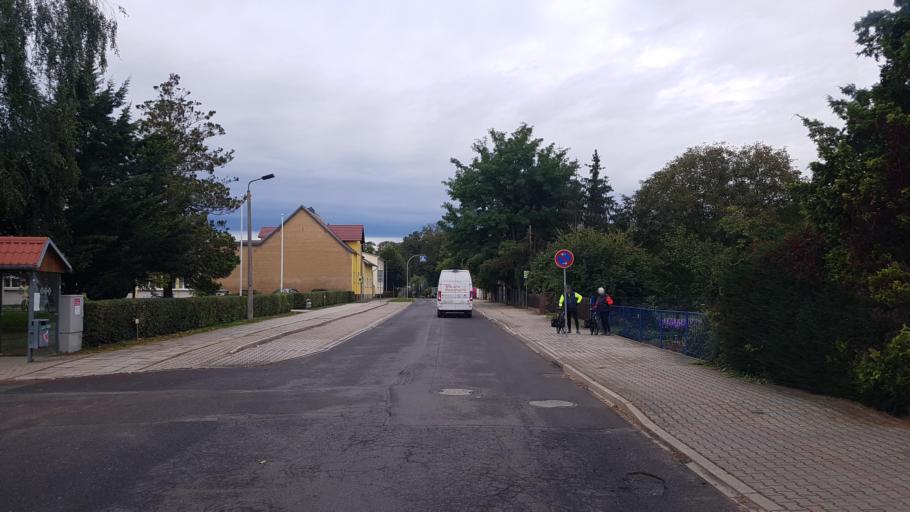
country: DE
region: Brandenburg
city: Golssen
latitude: 51.9713
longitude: 13.6009
